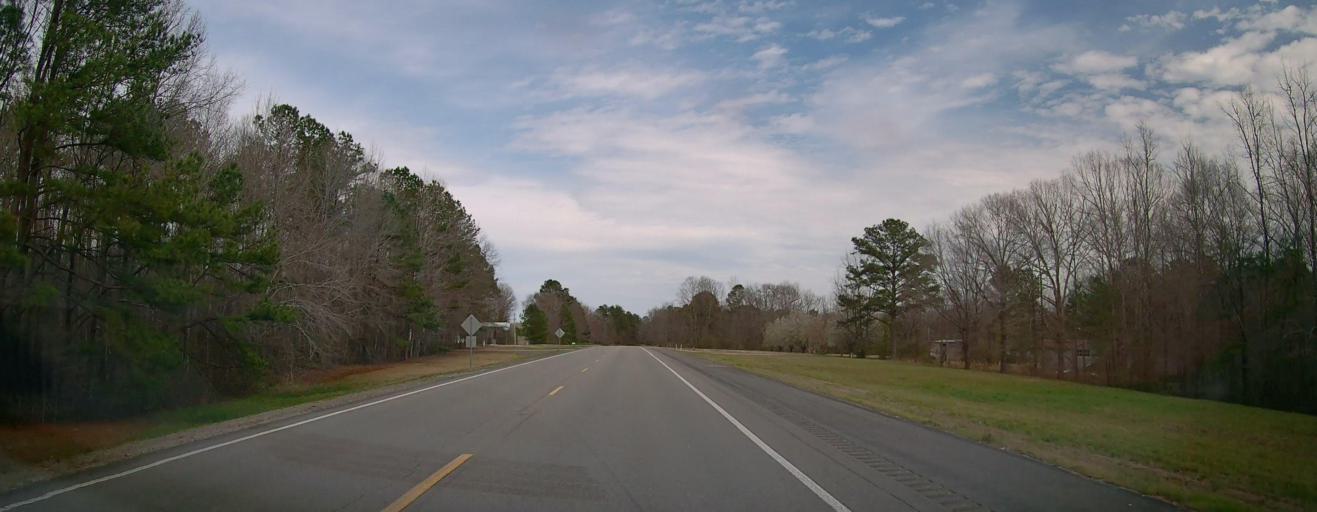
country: US
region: Alabama
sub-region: Marion County
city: Winfield
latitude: 33.9346
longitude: -87.7314
